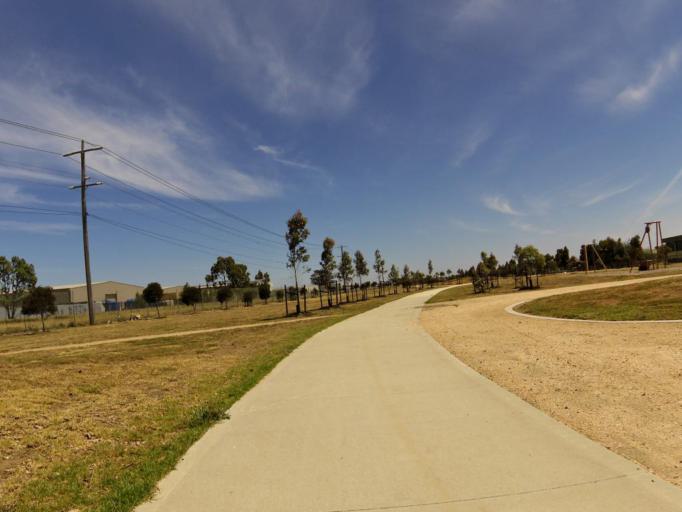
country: AU
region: Victoria
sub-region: Wyndham
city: Williams Landing
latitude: -37.8646
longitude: 144.7274
